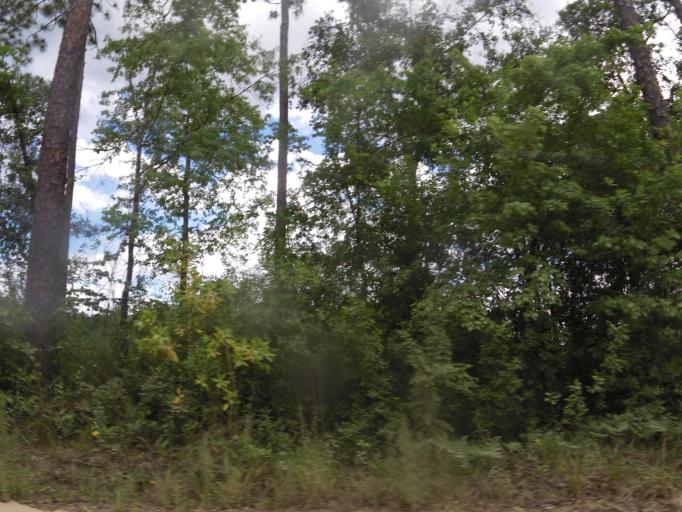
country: US
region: Florida
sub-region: Clay County
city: Asbury Lake
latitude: 29.9097
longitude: -81.7979
